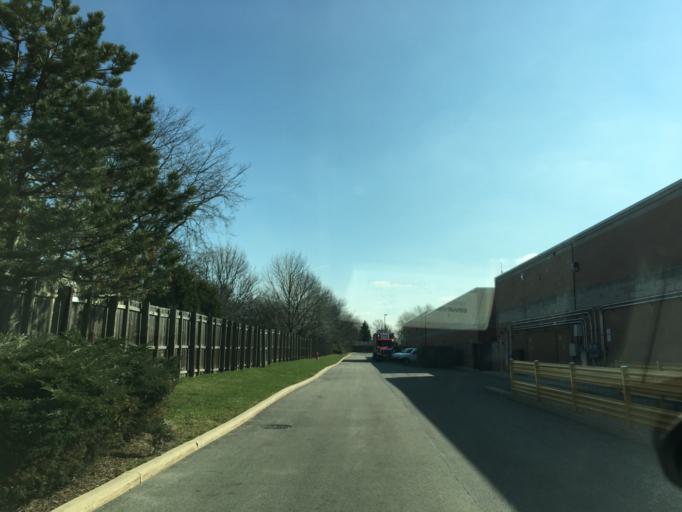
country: US
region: Illinois
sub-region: DuPage County
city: Hanover Park
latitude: 42.0194
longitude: -88.1435
